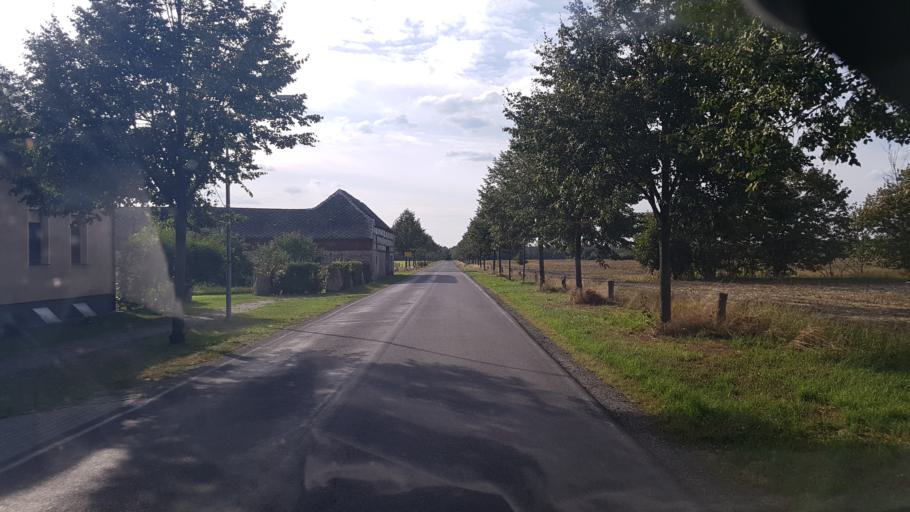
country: DE
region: Brandenburg
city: Welzow
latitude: 51.5522
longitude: 14.1826
